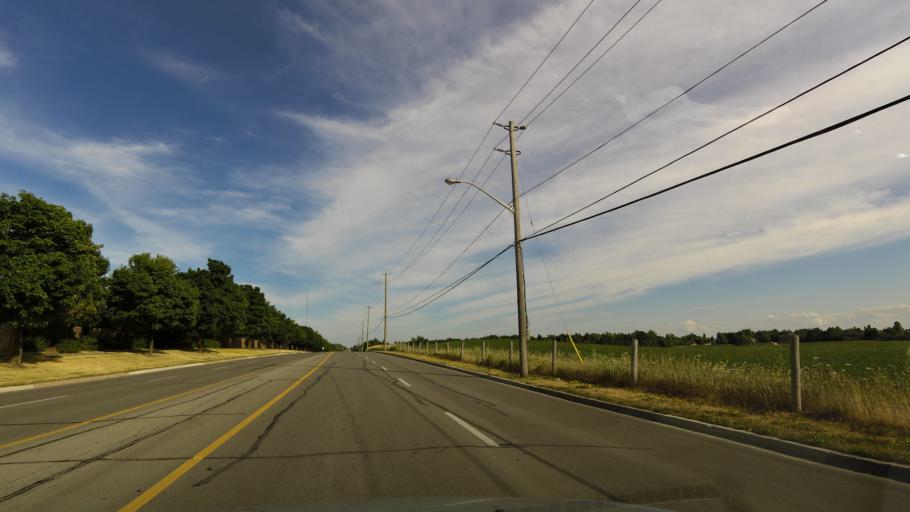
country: CA
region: Ontario
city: Brampton
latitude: 43.7419
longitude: -79.8122
